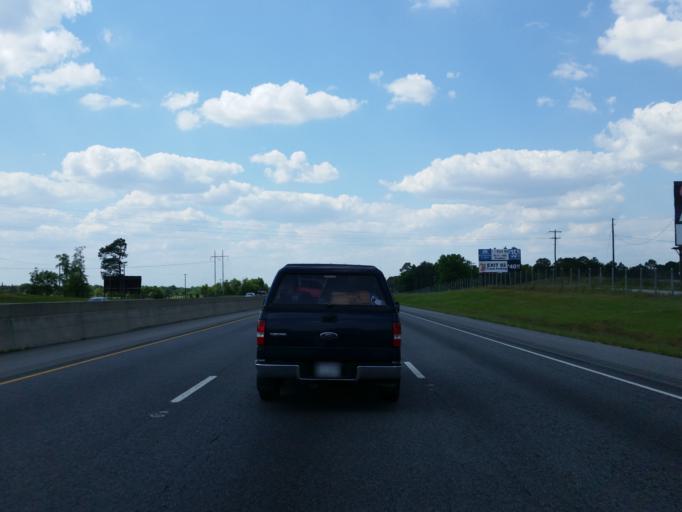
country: US
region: Georgia
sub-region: Tift County
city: Tifton
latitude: 31.5789
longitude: -83.5517
